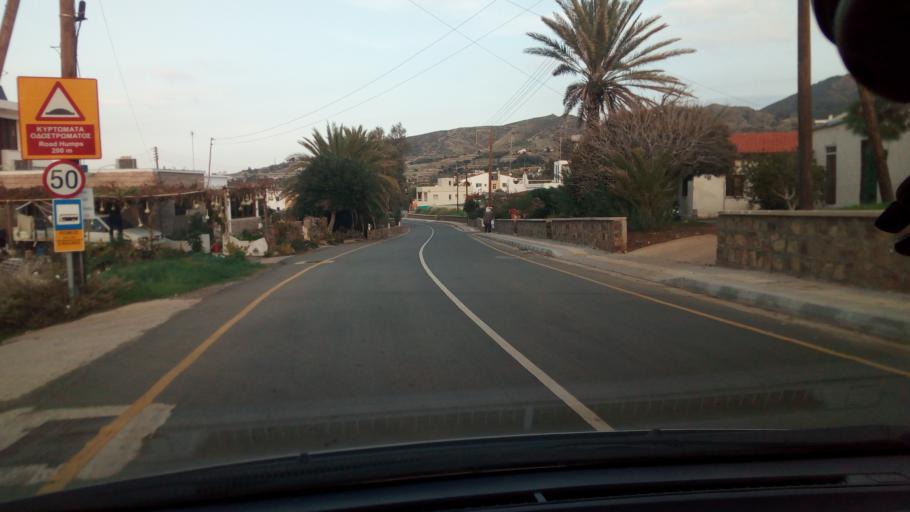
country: CY
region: Lefkosia
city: Kato Pyrgos
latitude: 35.1584
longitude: 32.5430
